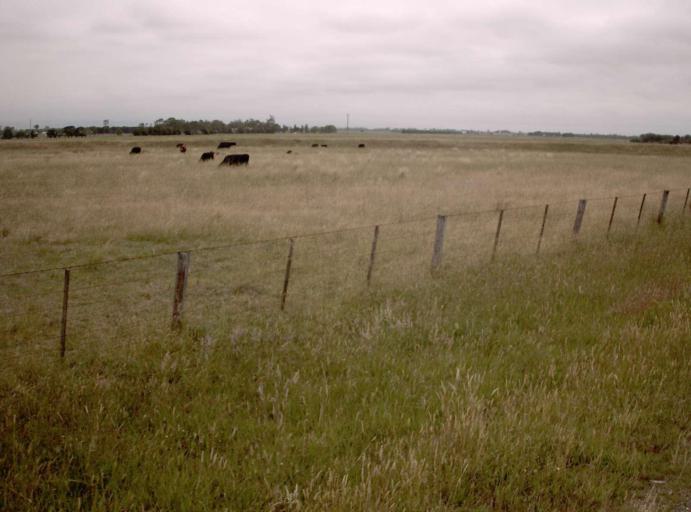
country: AU
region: Victoria
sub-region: Wellington
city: Heyfield
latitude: -38.1024
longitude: 146.7730
